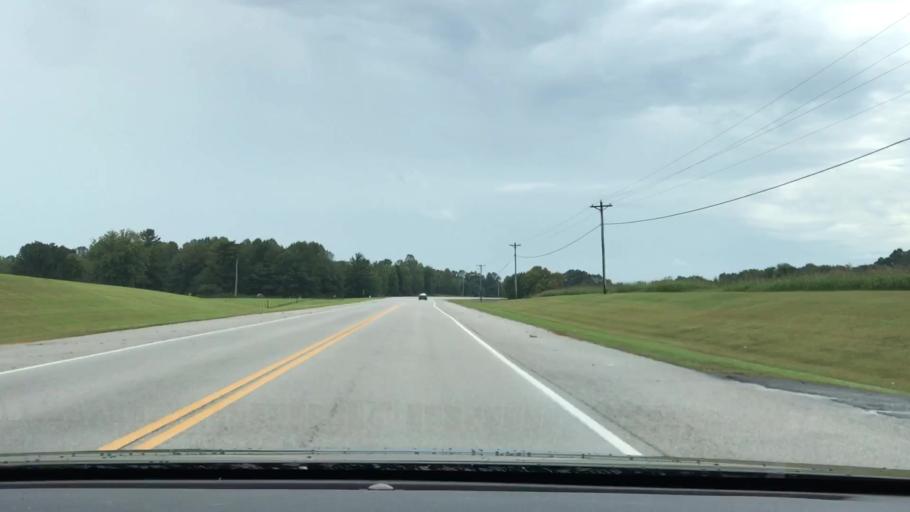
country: US
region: Tennessee
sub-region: Macon County
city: Red Boiling Springs
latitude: 36.5502
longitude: -85.8084
